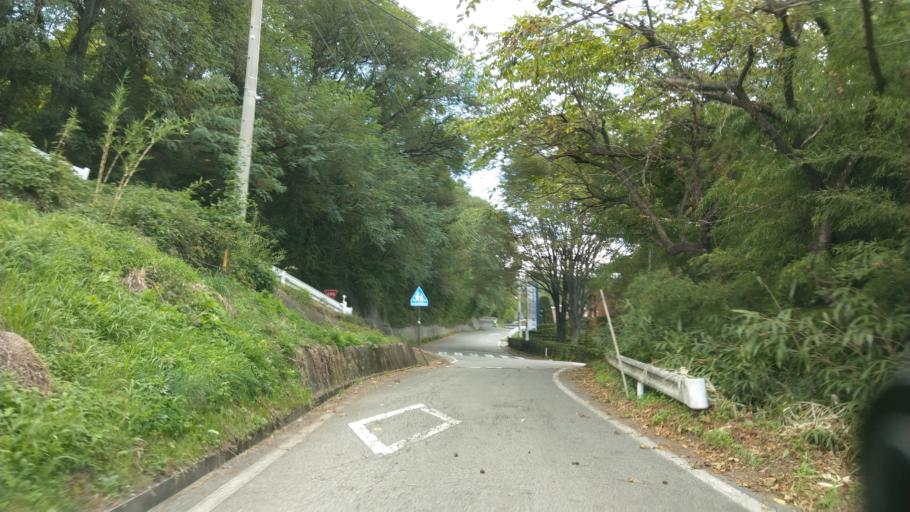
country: JP
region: Nagano
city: Komoro
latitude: 36.3497
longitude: 138.4115
